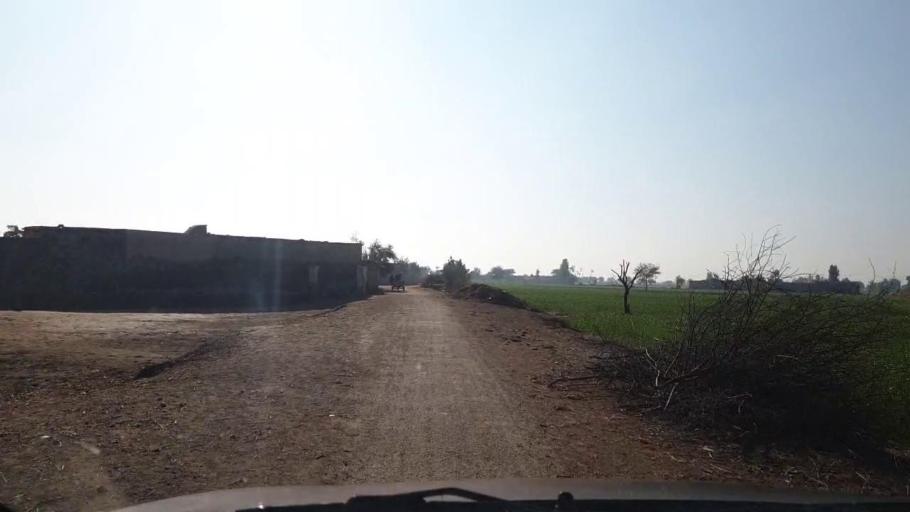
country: PK
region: Sindh
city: Sinjhoro
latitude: 26.0027
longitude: 68.7770
